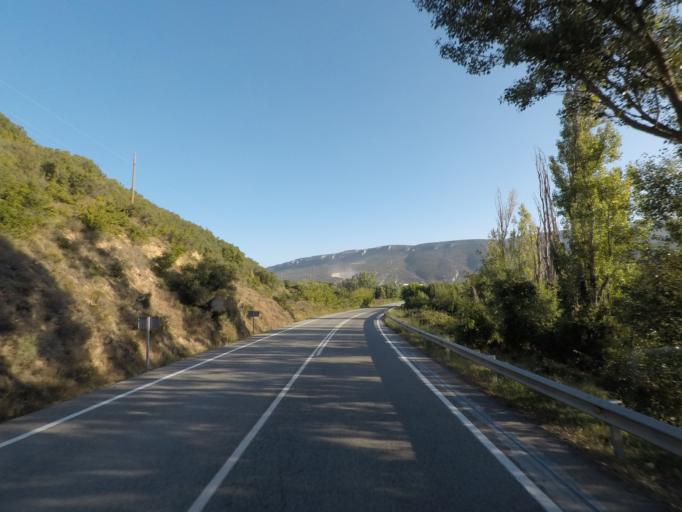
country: ES
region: Navarre
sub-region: Provincia de Navarra
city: Liedena
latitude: 42.6067
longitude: -1.2784
